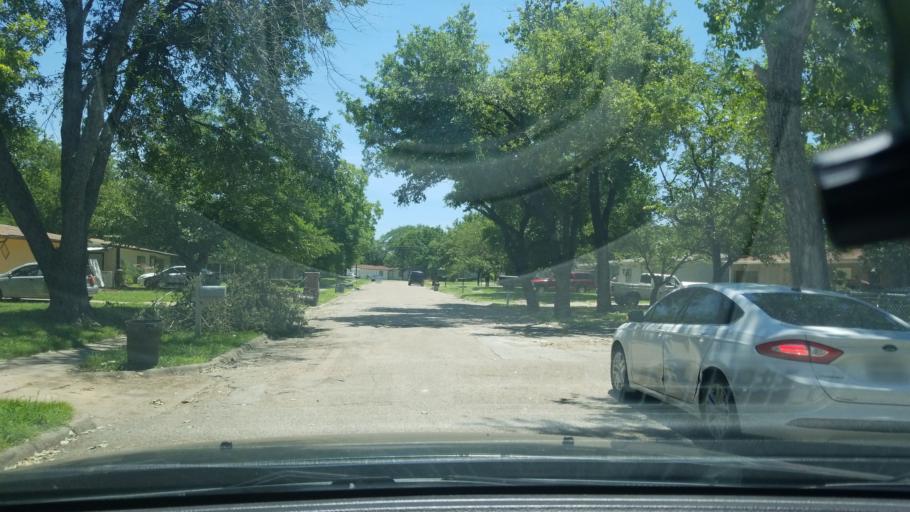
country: US
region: Texas
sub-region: Dallas County
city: Mesquite
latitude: 32.7814
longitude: -96.6028
